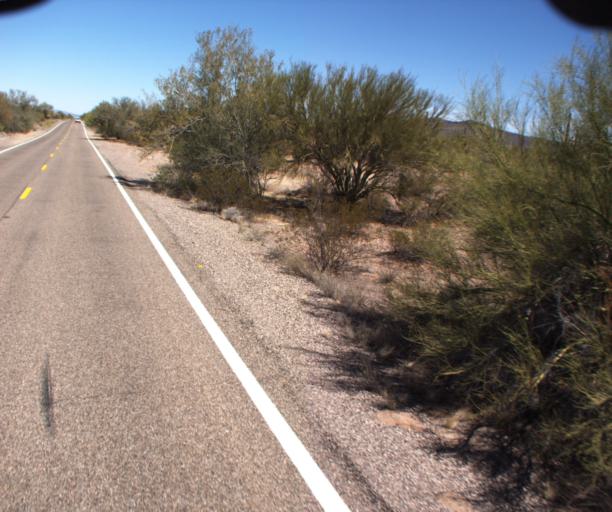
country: US
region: Arizona
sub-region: Pima County
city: Ajo
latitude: 32.1633
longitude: -112.7637
